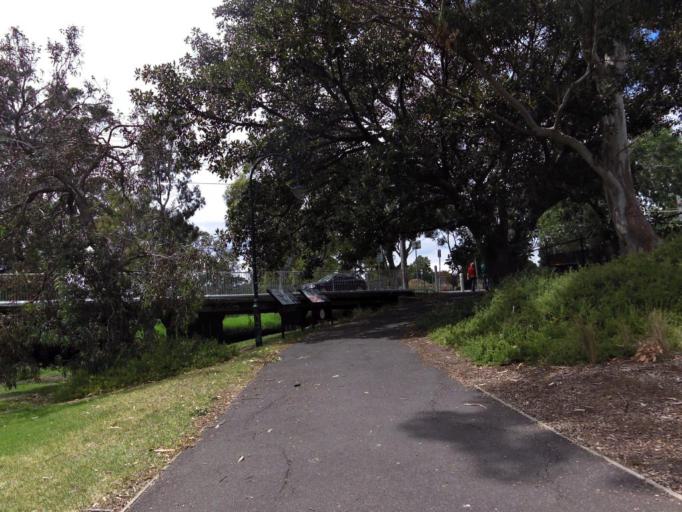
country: AU
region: Victoria
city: Ripponlea
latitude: -37.8859
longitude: 144.9914
